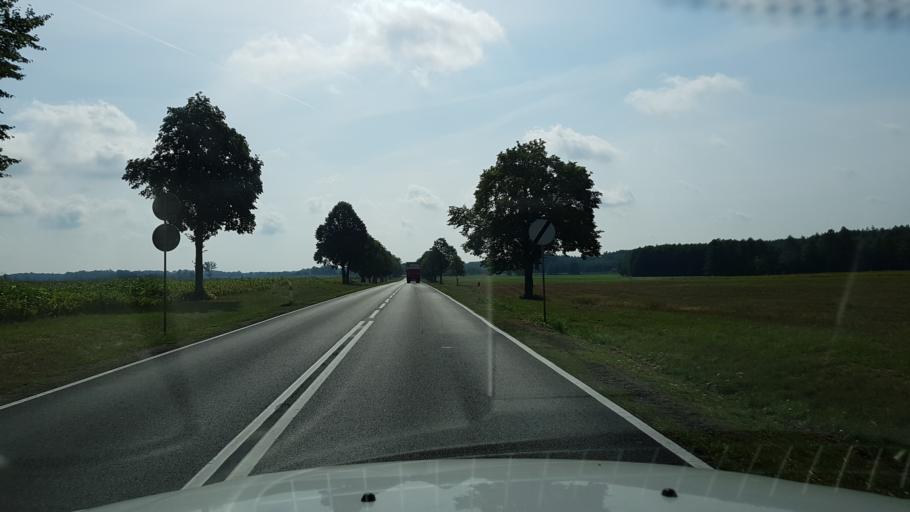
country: PL
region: West Pomeranian Voivodeship
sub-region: Powiat walecki
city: Walcz
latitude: 53.3265
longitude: 16.3063
